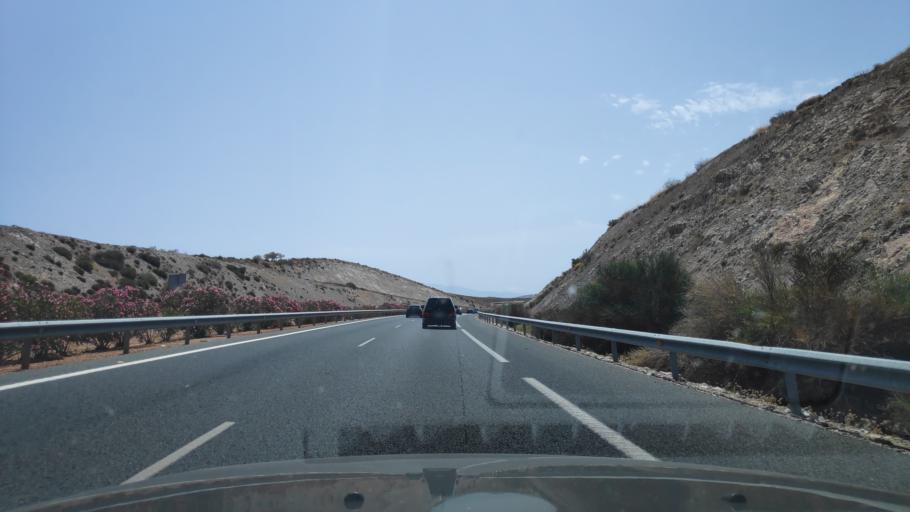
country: ES
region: Andalusia
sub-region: Provincia de Granada
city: Padul
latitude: 37.0022
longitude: -3.6329
